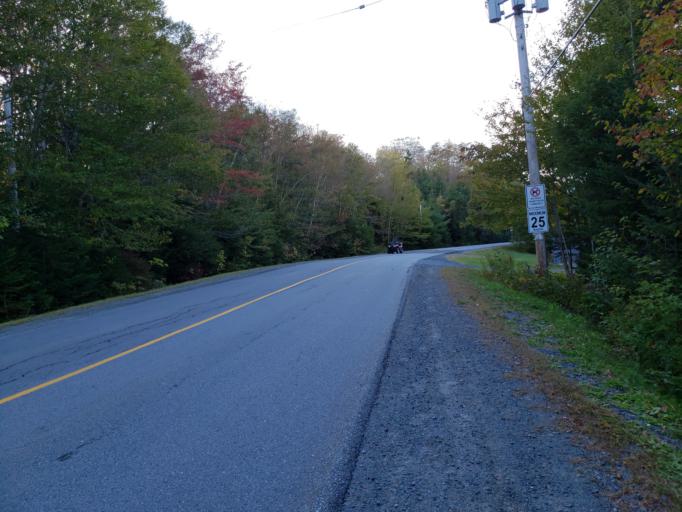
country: CA
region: Nova Scotia
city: Cole Harbour
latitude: 44.7435
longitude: -63.3794
